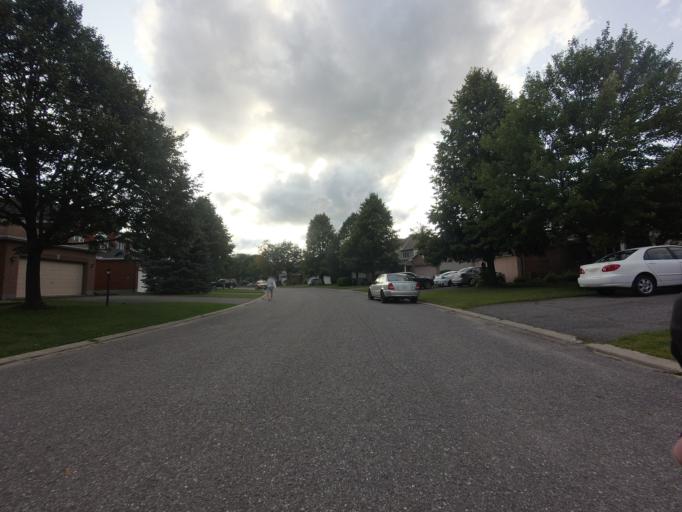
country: CA
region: Ontario
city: Bells Corners
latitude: 45.2848
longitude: -75.7170
